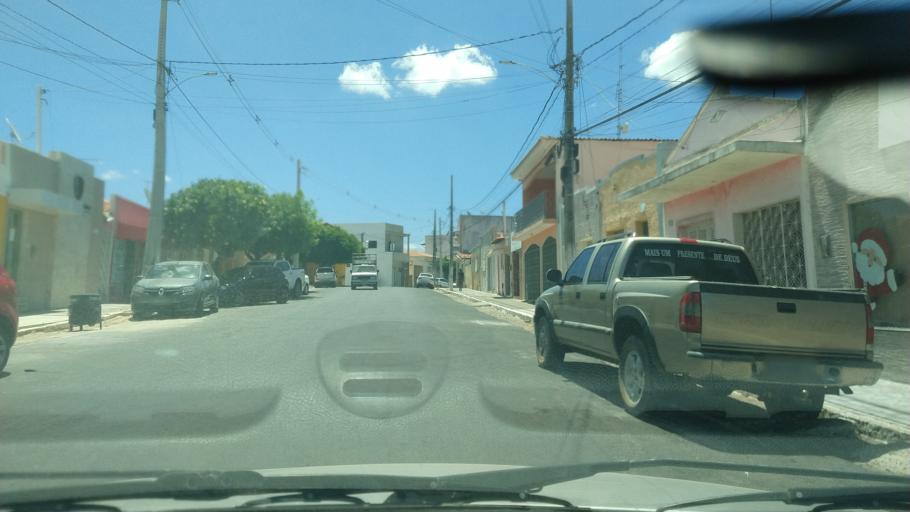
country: BR
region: Rio Grande do Norte
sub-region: Cerro Cora
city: Cerro Cora
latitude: -6.0463
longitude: -36.3467
